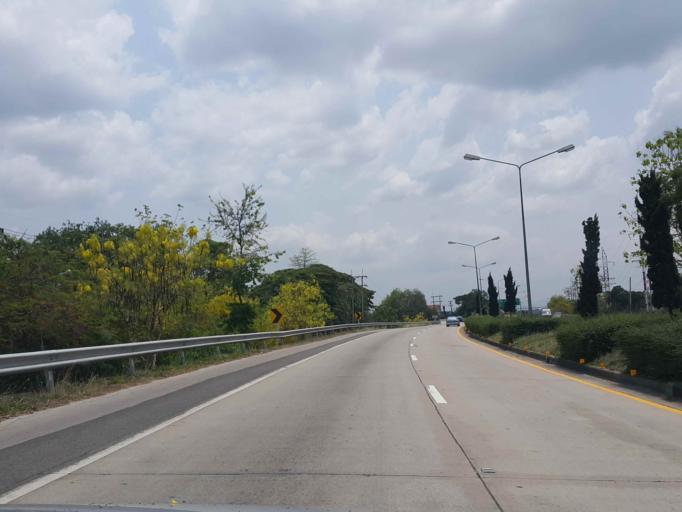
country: TH
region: Lampang
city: Lampang
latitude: 18.2717
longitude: 99.4622
